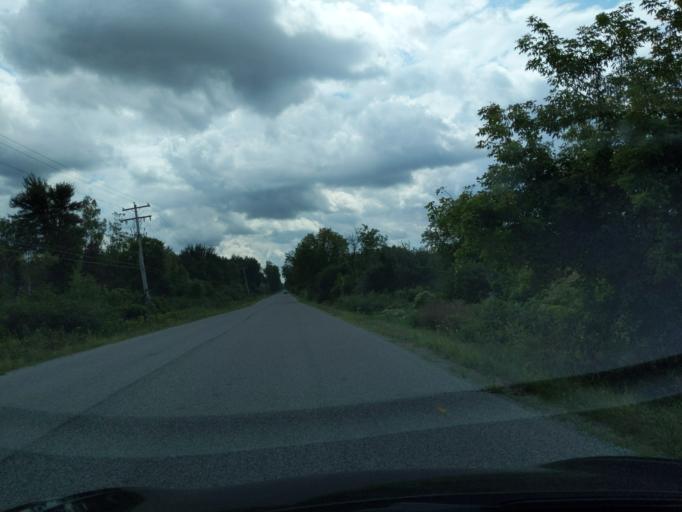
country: US
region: Michigan
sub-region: Eaton County
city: Dimondale
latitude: 42.6504
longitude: -84.5825
